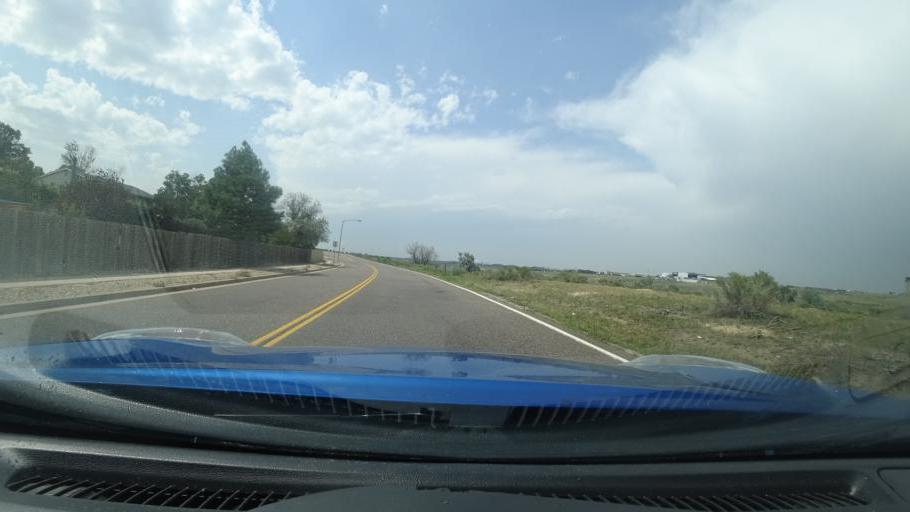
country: US
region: Colorado
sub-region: Adams County
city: Aurora
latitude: 39.6950
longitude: -104.7640
